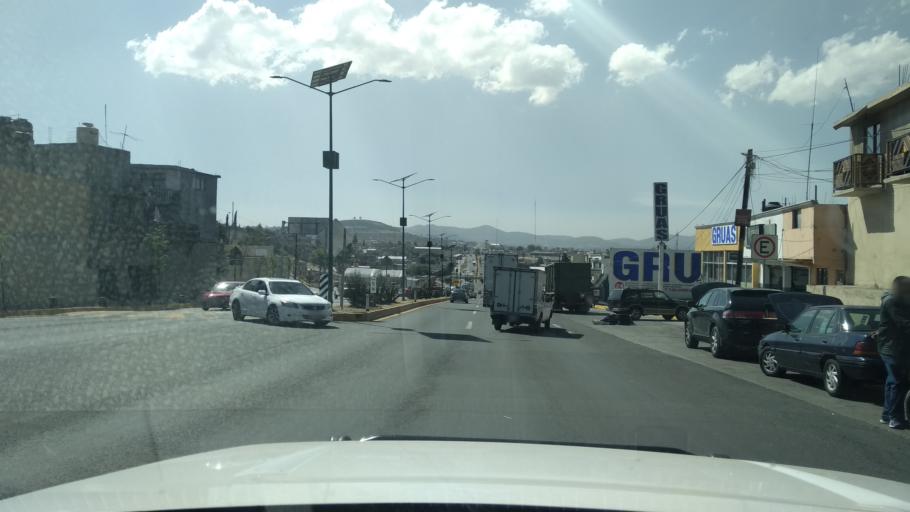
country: MX
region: Hidalgo
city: Calpulalpan
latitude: 19.5922
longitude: -98.5672
